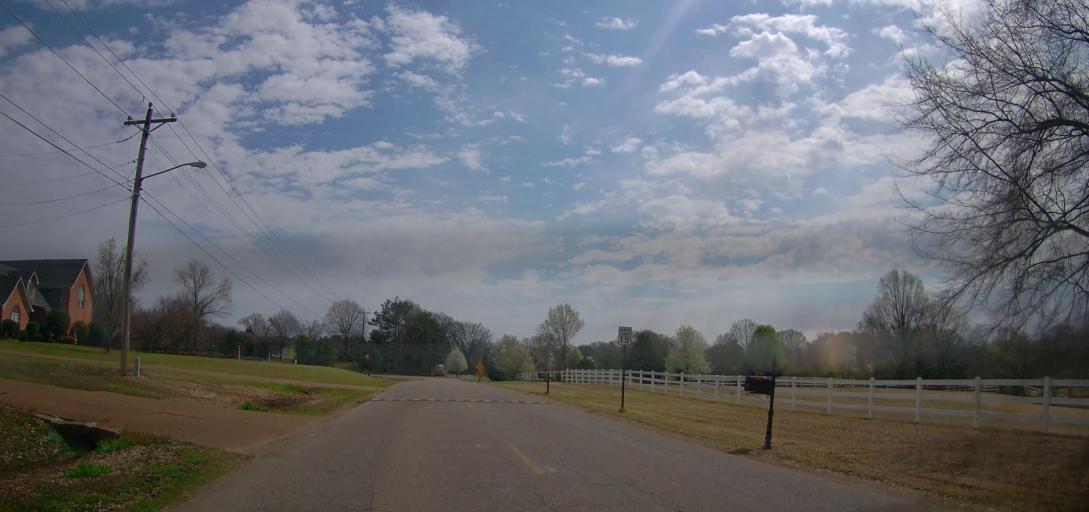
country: US
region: Mississippi
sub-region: De Soto County
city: Olive Branch
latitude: 34.9913
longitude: -89.8501
